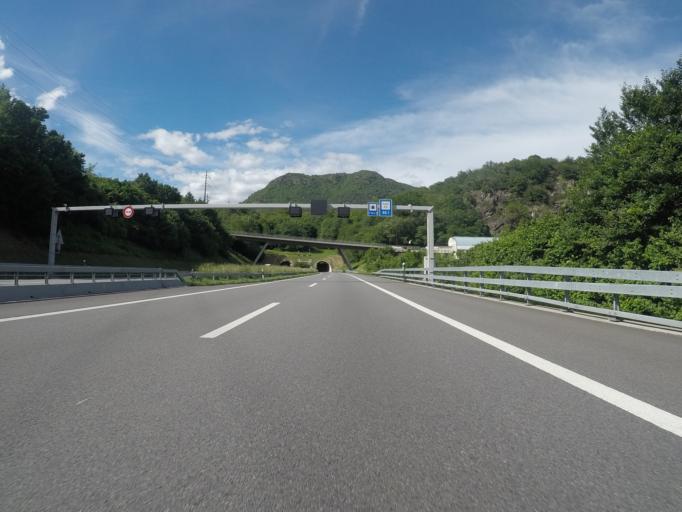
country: CH
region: Ticino
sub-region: Lugano District
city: Gravesano
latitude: 46.0664
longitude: 8.9285
